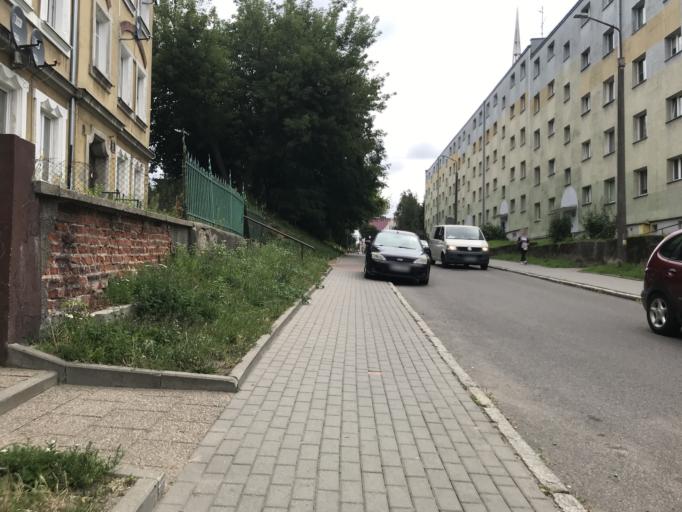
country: PL
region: Warmian-Masurian Voivodeship
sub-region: Powiat elblaski
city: Elblag
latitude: 54.1711
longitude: 19.3995
